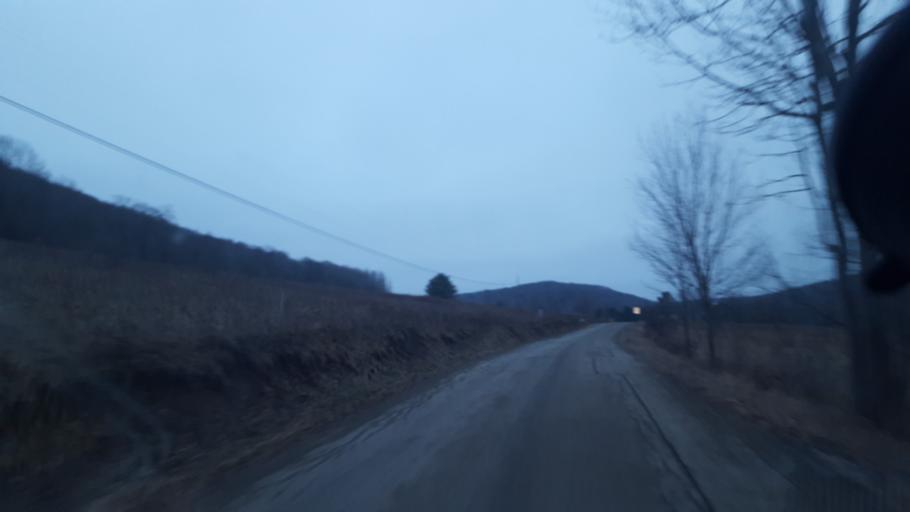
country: US
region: Pennsylvania
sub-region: Tioga County
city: Westfield
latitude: 41.9562
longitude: -77.6993
